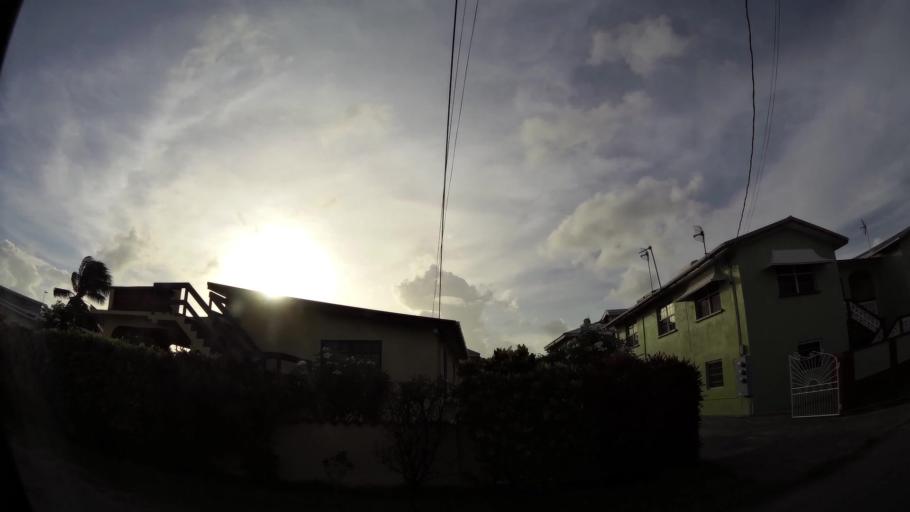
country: BB
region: Christ Church
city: Oistins
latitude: 13.0577
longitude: -59.5110
